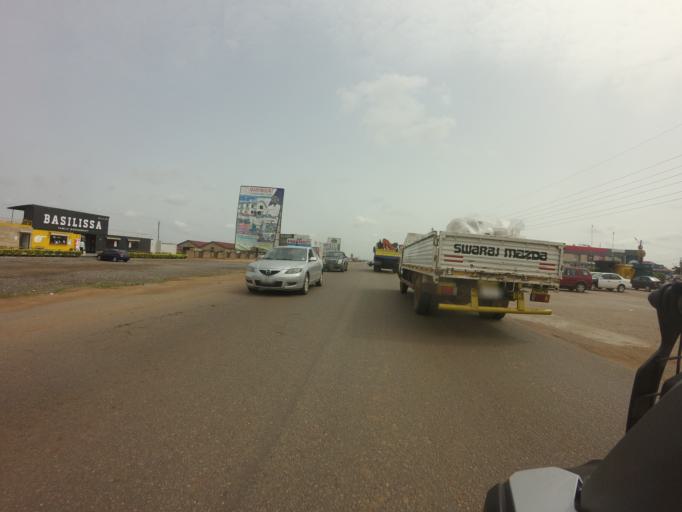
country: GH
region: Greater Accra
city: Tema
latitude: 5.7379
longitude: 0.0327
